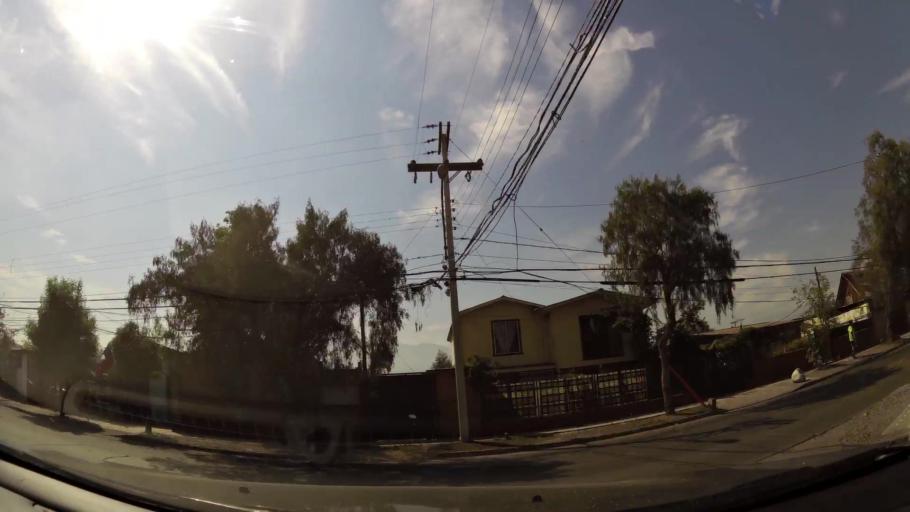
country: CL
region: Santiago Metropolitan
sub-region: Provincia de Santiago
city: La Pintana
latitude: -33.5670
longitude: -70.5963
